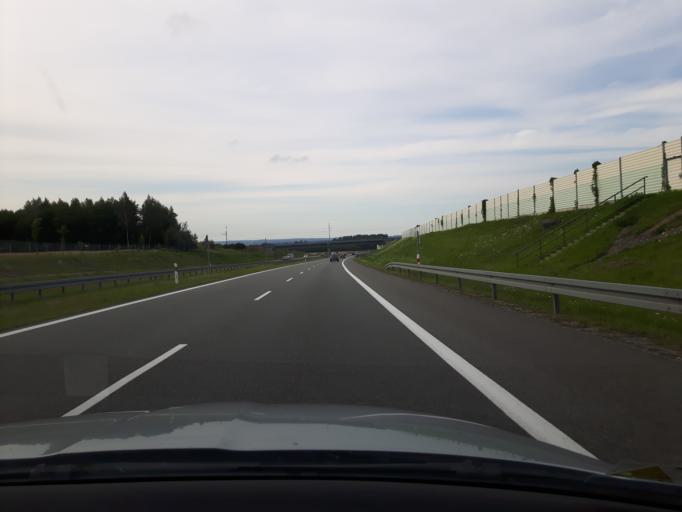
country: PL
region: Warmian-Masurian Voivodeship
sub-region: Powiat elblaski
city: Paslek
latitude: 54.0155
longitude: 19.6766
